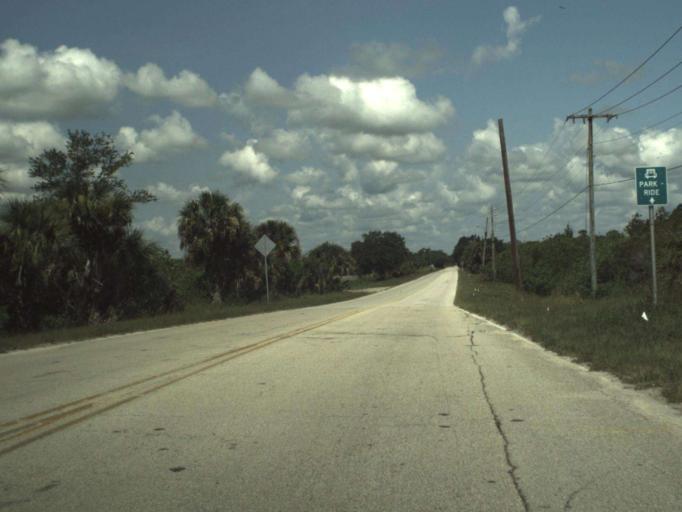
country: US
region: Florida
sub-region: Brevard County
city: June Park
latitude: 28.1205
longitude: -80.7088
